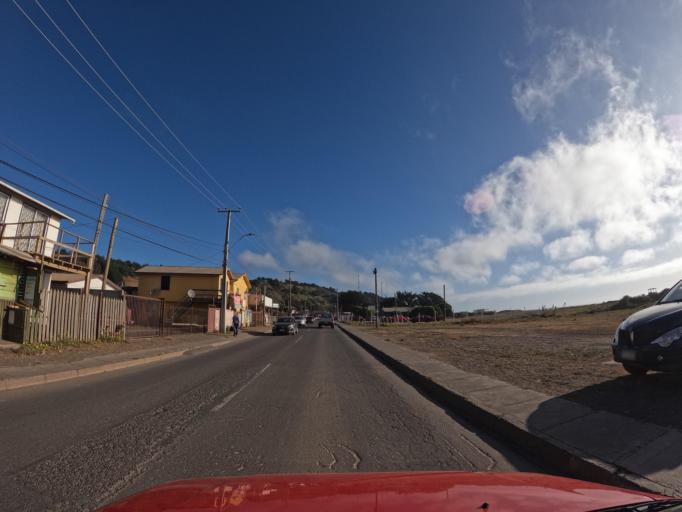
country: CL
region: Maule
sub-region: Provincia de Talca
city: Constitucion
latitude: -34.9333
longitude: -72.1805
